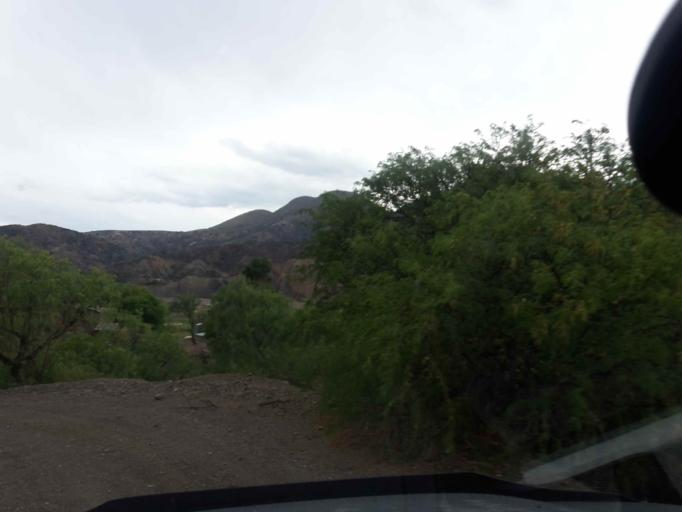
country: BO
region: Cochabamba
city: Sipe Sipe
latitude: -17.5317
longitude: -66.5154
